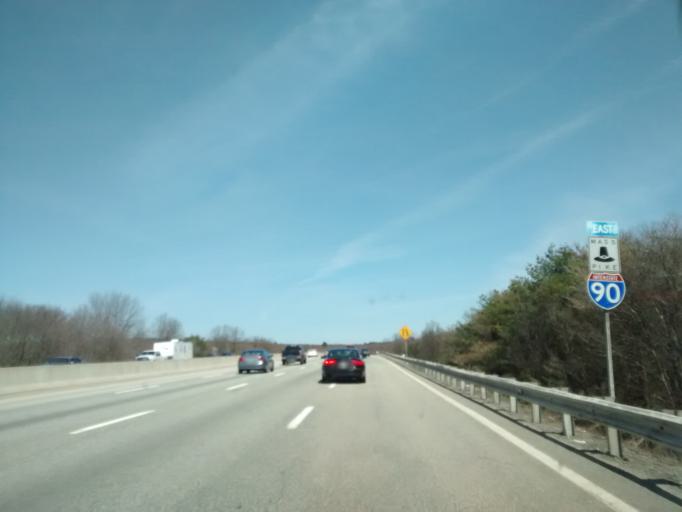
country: US
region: Massachusetts
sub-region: Worcester County
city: Cordaville
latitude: 42.2673
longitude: -71.5626
